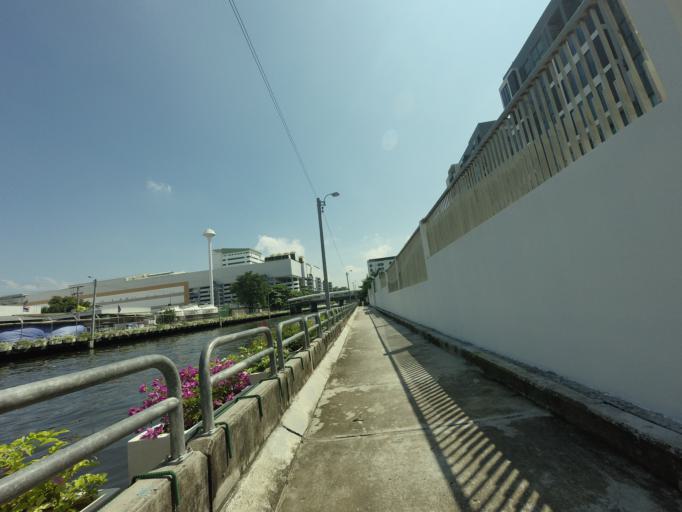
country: TH
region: Bangkok
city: Bang Kapi
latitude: 13.7640
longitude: 100.6403
